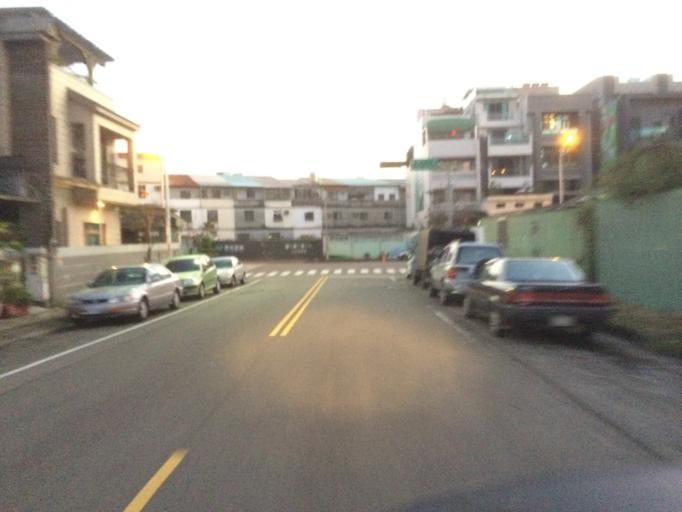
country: TW
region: Taiwan
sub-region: Taichung City
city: Taichung
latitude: 24.1788
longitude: 120.7178
